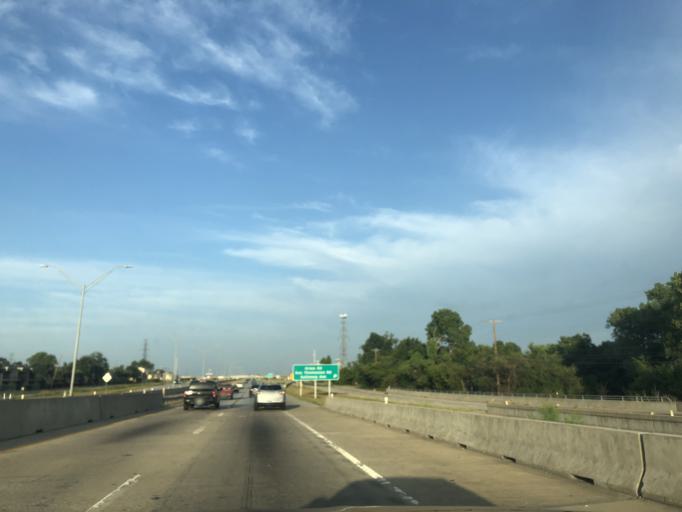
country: US
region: Texas
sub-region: Dallas County
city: Mesquite
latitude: 32.7923
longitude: -96.6430
